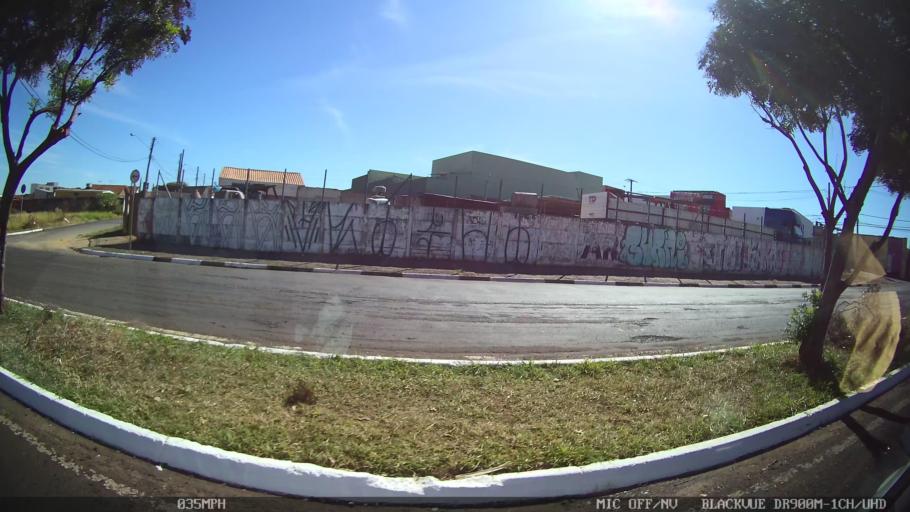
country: BR
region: Sao Paulo
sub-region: Franca
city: Franca
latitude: -20.5403
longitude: -47.3634
